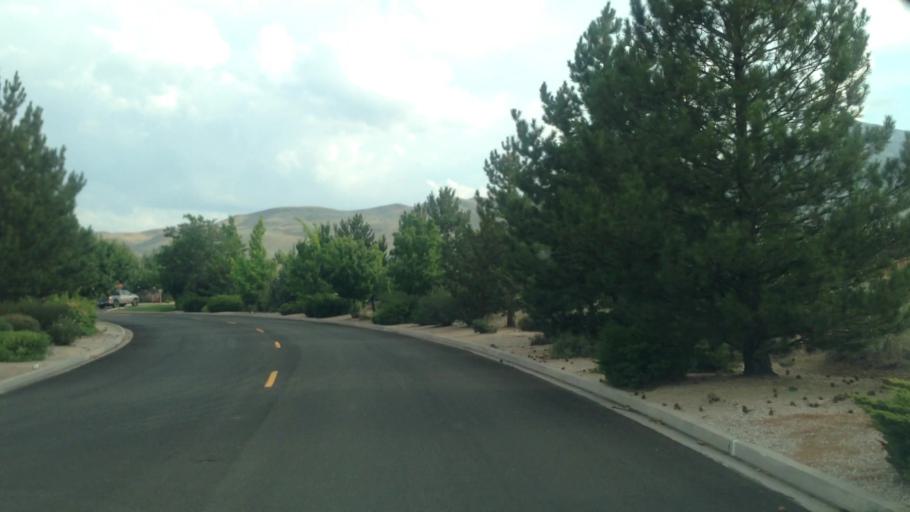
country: US
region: Nevada
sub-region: Washoe County
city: Lemmon Valley
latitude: 39.6268
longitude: -119.8757
